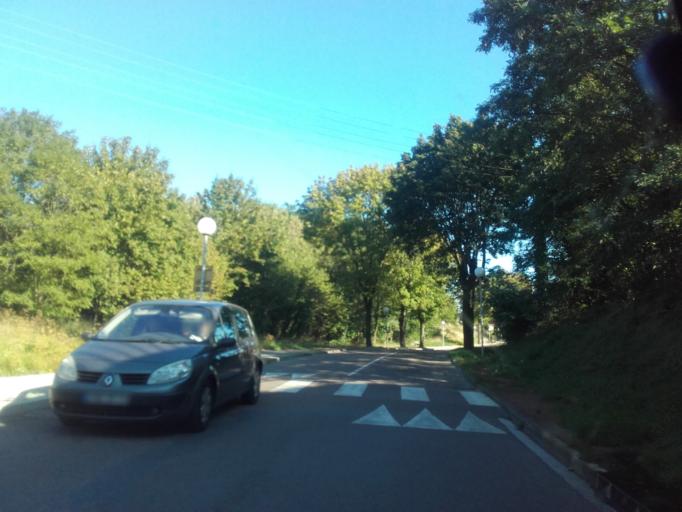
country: FR
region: Bourgogne
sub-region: Departement de Saone-et-Loire
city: Chagny
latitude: 46.9118
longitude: 4.7583
